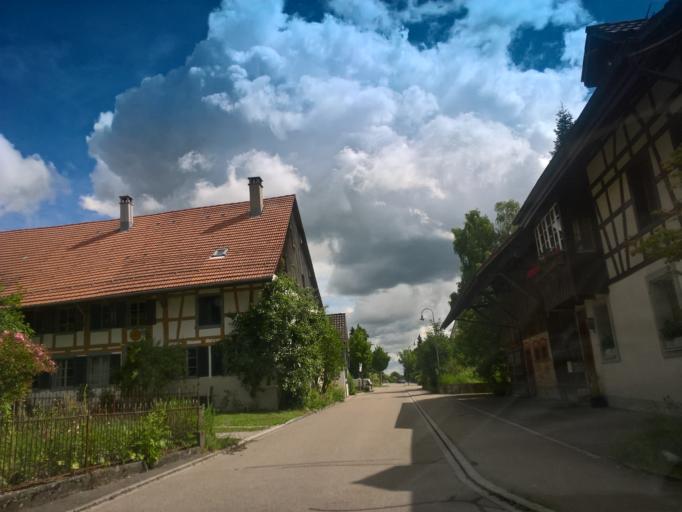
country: CH
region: Zurich
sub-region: Bezirk Winterthur
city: Brutten
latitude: 47.4743
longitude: 8.6758
